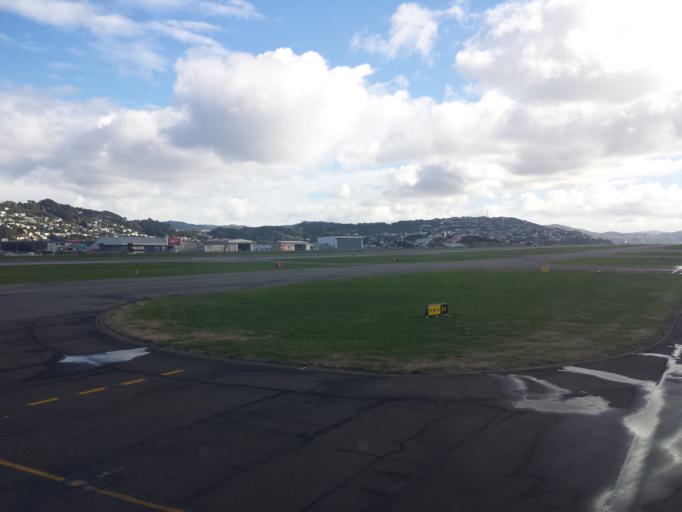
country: NZ
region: Wellington
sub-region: Wellington City
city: Wellington
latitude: -41.3310
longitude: 174.8086
